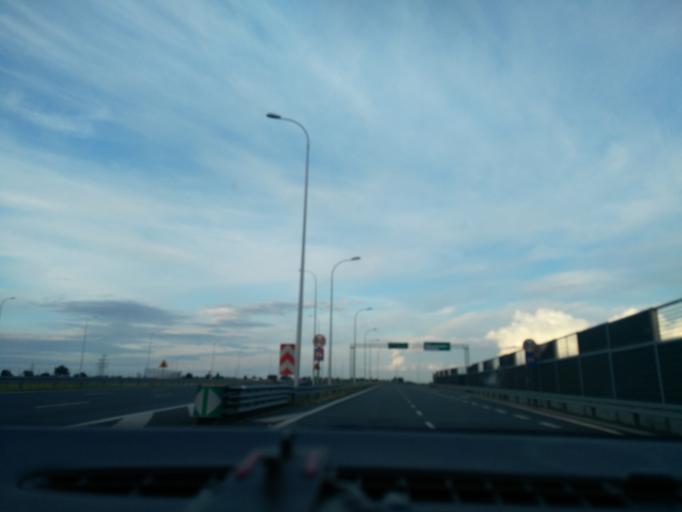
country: PL
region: Lublin Voivodeship
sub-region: Powiat lubelski
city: Lublin
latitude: 51.3027
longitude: 22.5797
